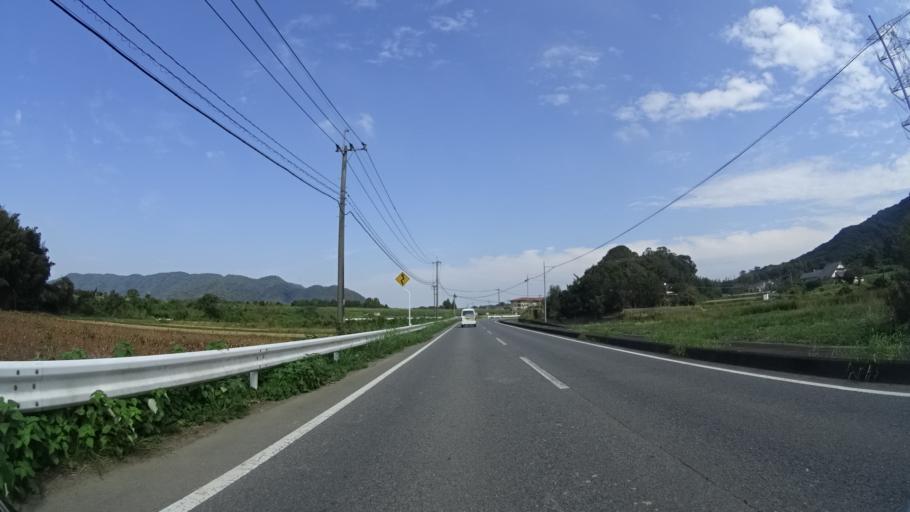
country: JP
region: Kumamoto
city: Matsubase
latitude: 32.6619
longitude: 130.7162
